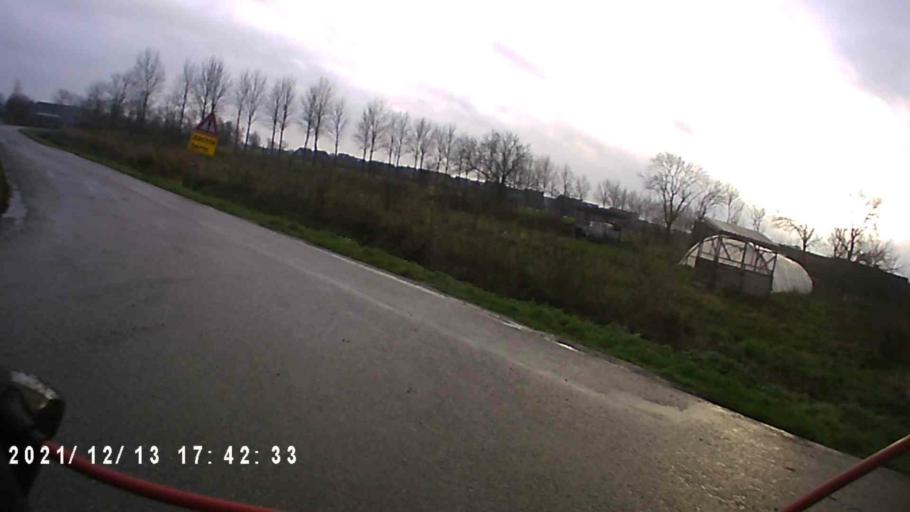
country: NL
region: Groningen
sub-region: Gemeente Bedum
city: Bedum
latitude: 53.2865
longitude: 6.7058
